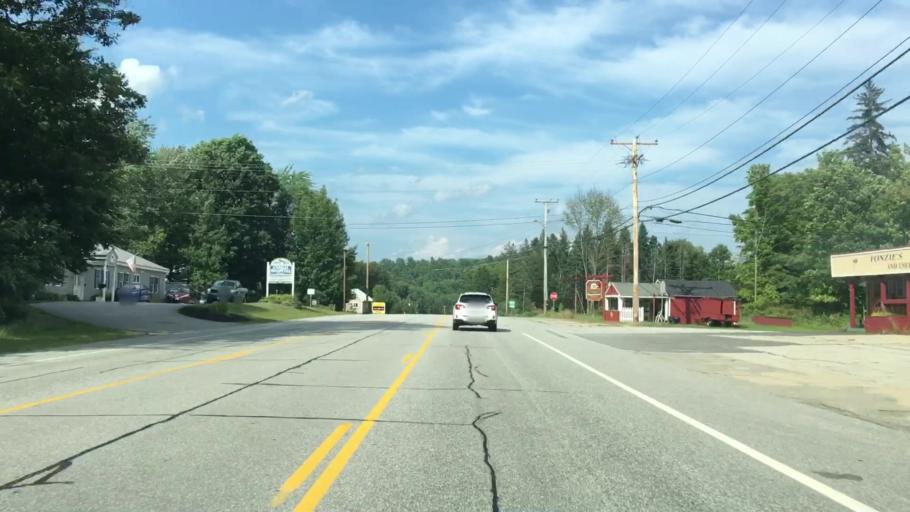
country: US
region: New Hampshire
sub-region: Belknap County
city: Sanbornton
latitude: 43.4793
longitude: -71.5412
